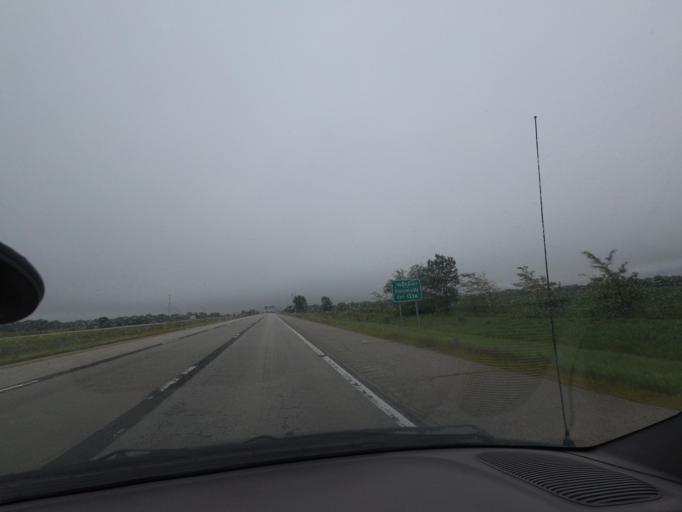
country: US
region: Illinois
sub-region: Macon County
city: Harristown
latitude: 39.8349
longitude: -89.0635
